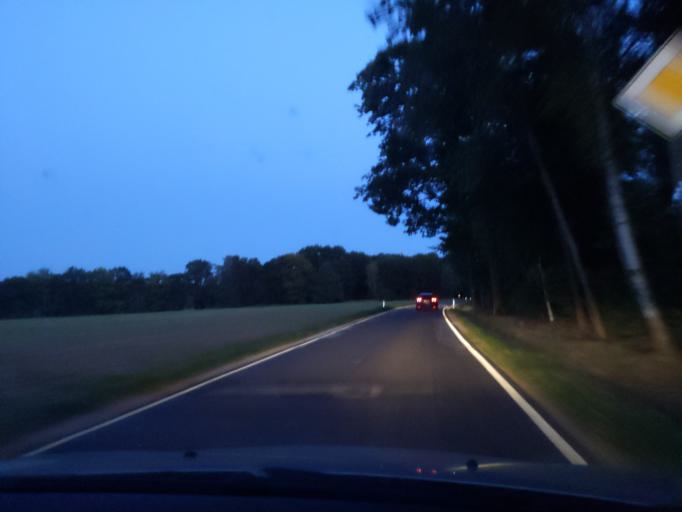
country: DE
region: Saxony
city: Grossdubrau
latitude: 51.2879
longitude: 14.4771
